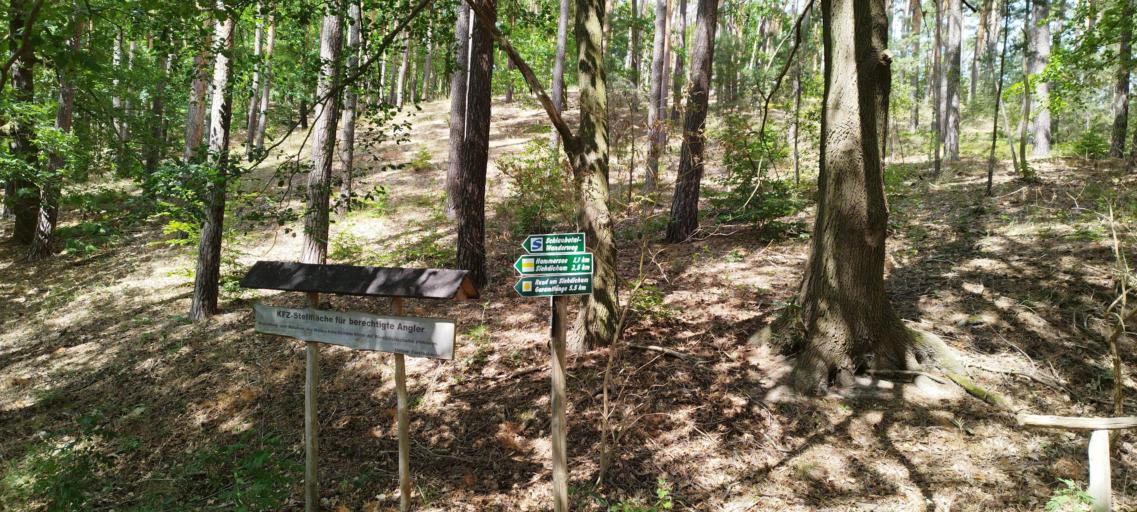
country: DE
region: Brandenburg
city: Mixdorf
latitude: 52.1554
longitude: 14.4576
